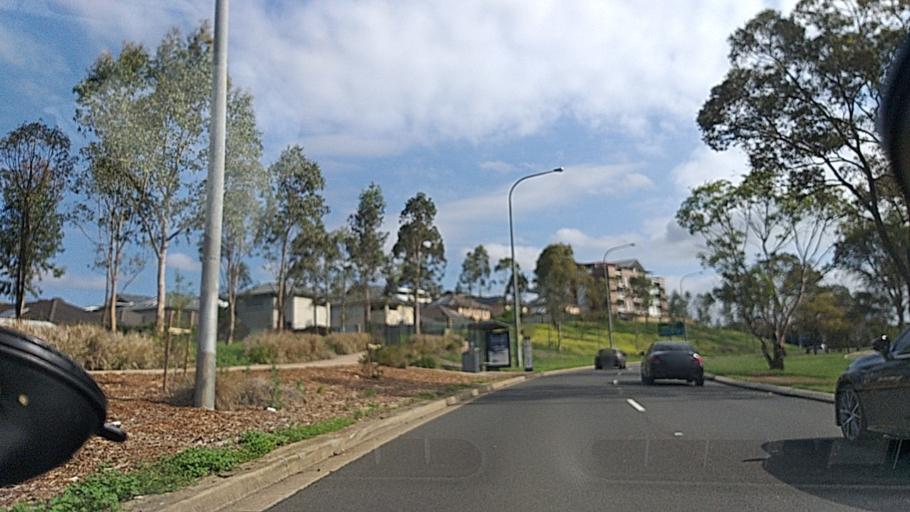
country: AU
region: New South Wales
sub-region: Campbelltown Municipality
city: Glen Alpine
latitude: -34.0771
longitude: 150.7996
